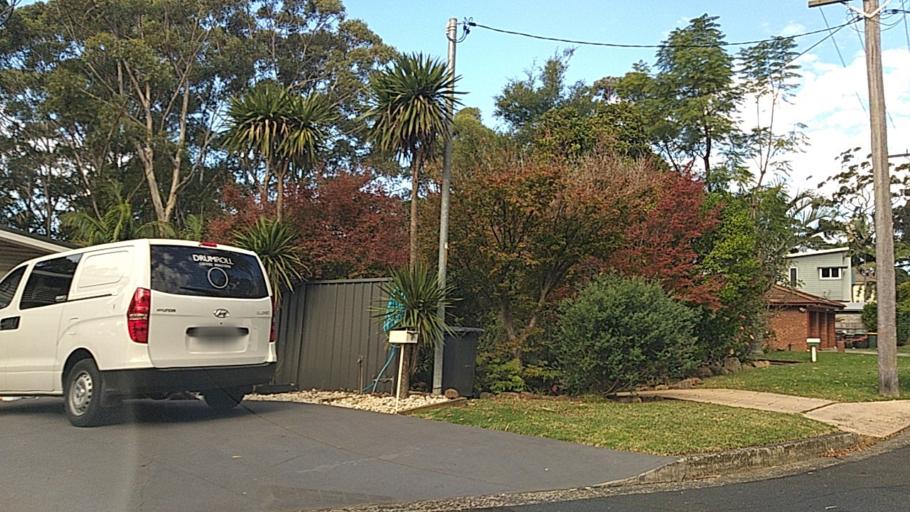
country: AU
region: New South Wales
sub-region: Wollongong
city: Bulli
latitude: -34.3317
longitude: 150.8998
